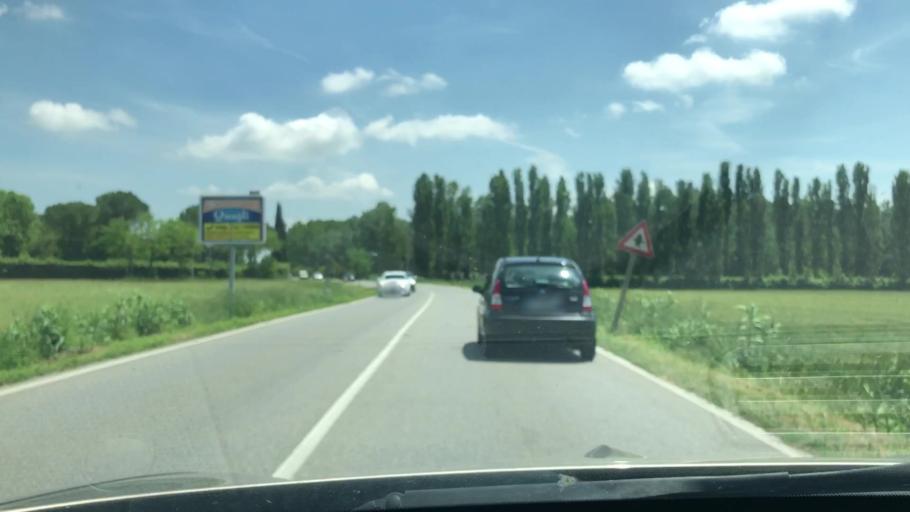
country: IT
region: Tuscany
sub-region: Province of Pisa
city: Treggiaia
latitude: 43.6160
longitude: 10.6776
